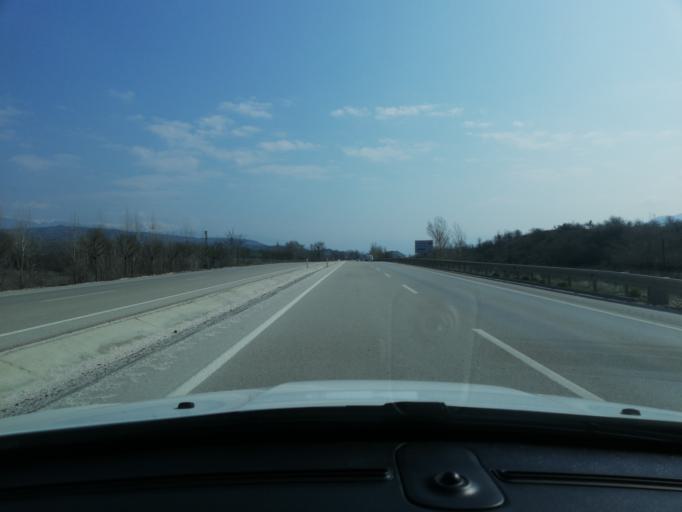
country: TR
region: Cankiri
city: Beloren
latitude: 40.8711
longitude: 33.4949
